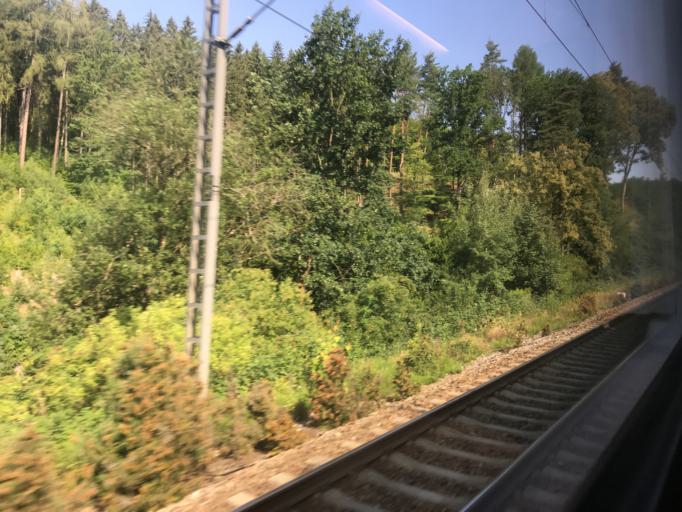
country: CZ
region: Central Bohemia
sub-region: Okres Benesov
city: Cercany
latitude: 49.8828
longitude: 14.7267
